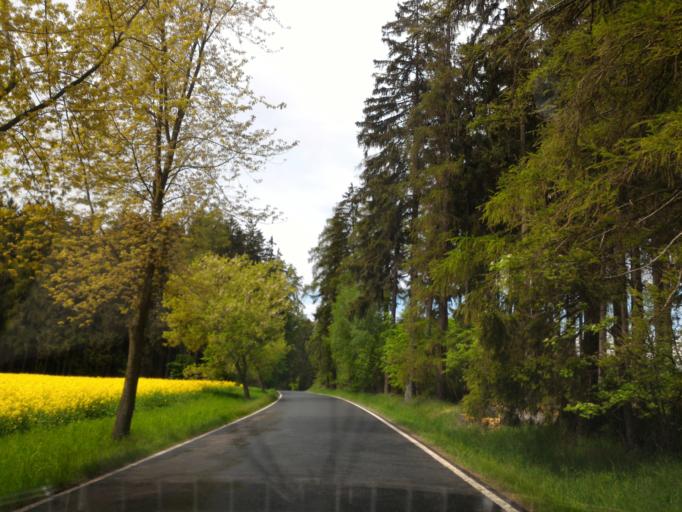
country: CZ
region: Vysocina
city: Ledec nad Sazavou
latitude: 49.7730
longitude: 15.2563
